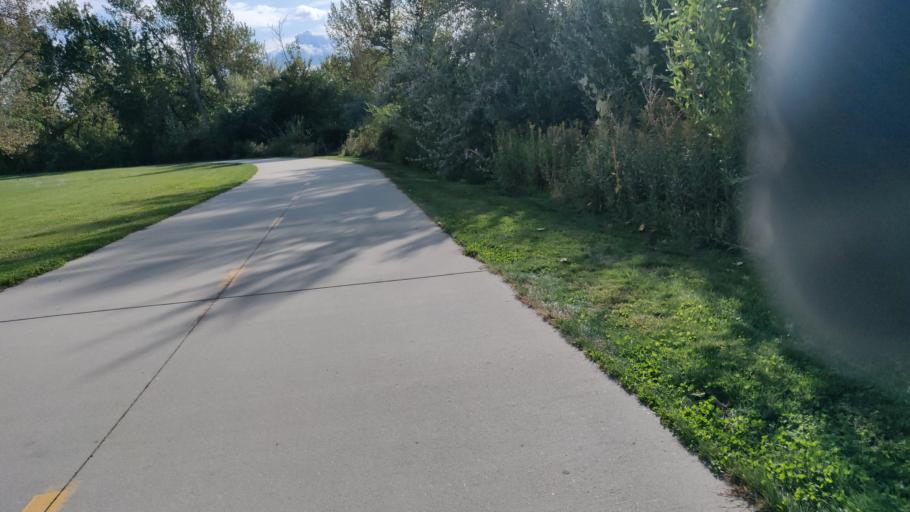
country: US
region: Idaho
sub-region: Ada County
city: Boise
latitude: 43.5775
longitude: -116.1515
